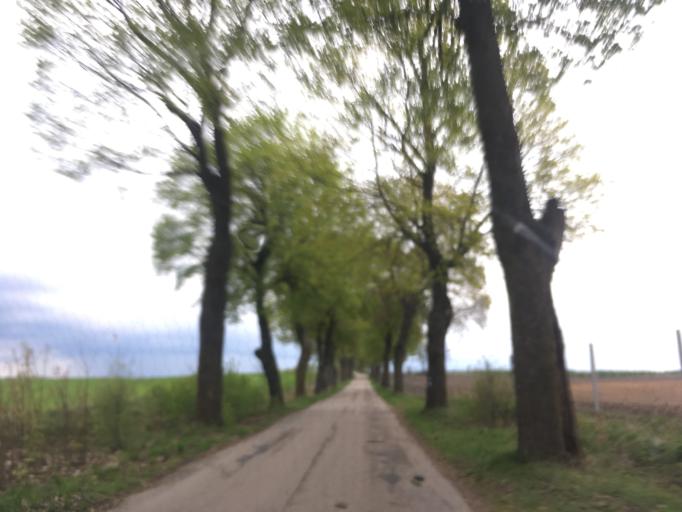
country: PL
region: Warmian-Masurian Voivodeship
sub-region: Powiat ostrodzki
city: Dabrowno
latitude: 53.4137
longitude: 20.1367
